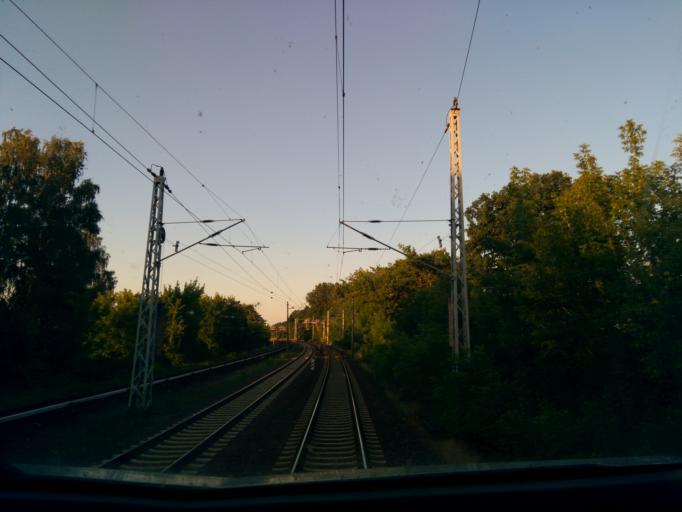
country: DE
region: Brandenburg
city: Wildau
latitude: 52.3168
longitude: 13.6324
